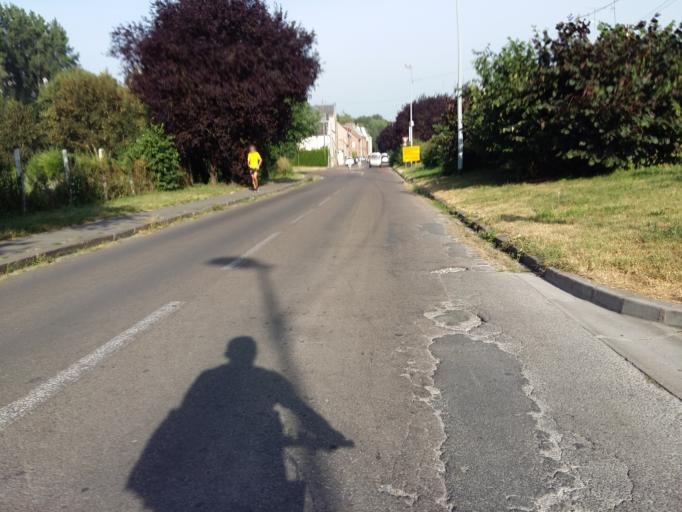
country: FR
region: Picardie
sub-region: Departement de la Somme
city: Rivery
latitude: 49.8994
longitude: 2.3186
